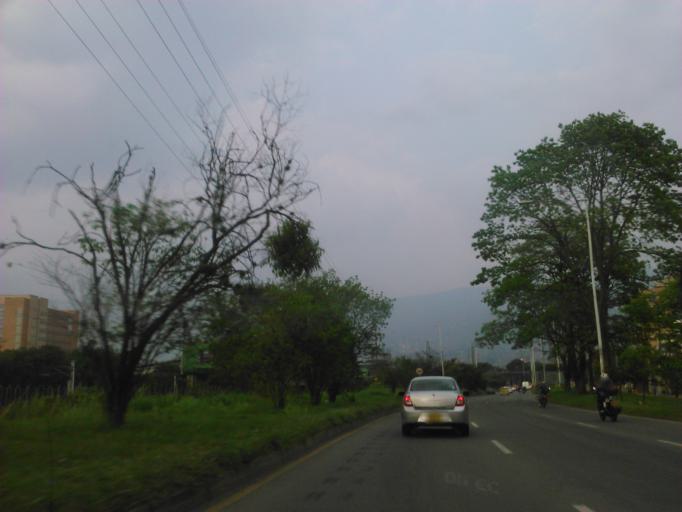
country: CO
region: Antioquia
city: Sabaneta
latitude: 6.1616
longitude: -75.6090
